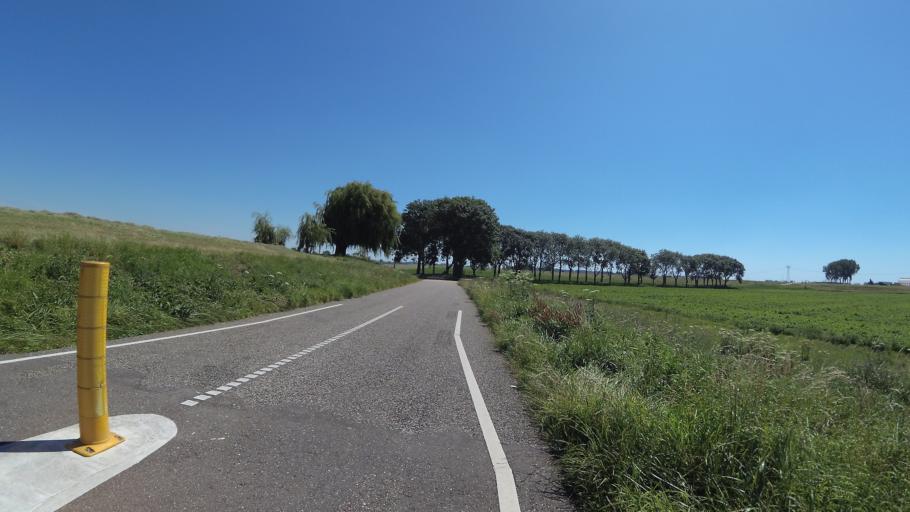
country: NL
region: North Brabant
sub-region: Gemeente Waalwijk
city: Waspik
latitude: 51.7141
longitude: 4.9823
